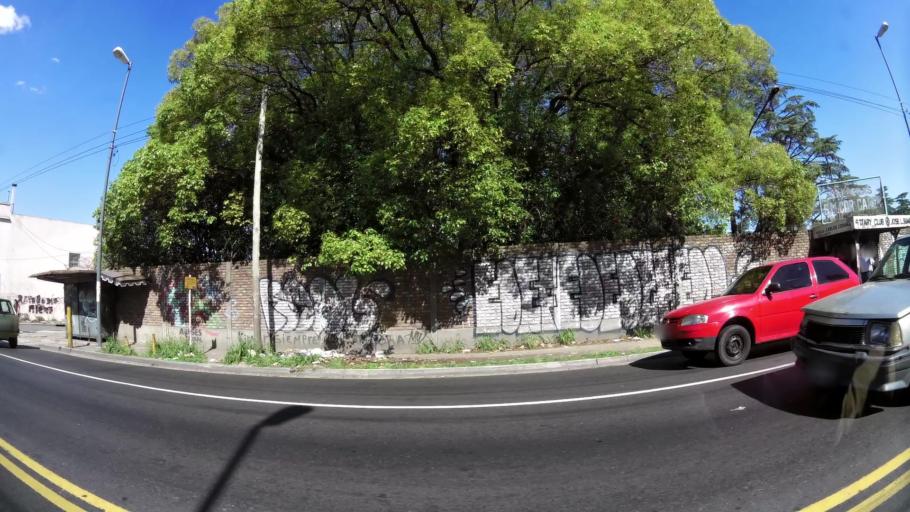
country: AR
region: Buenos Aires
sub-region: Partido de General San Martin
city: General San Martin
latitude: -34.5247
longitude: -58.5719
